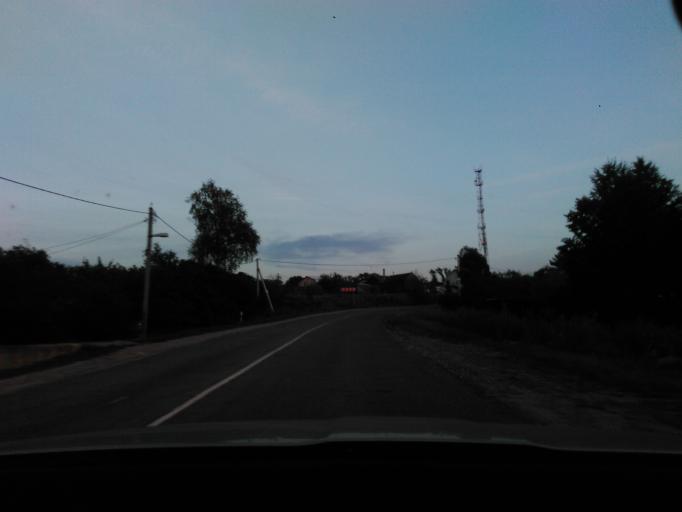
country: RU
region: Moskovskaya
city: Klin
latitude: 56.2517
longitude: 36.7602
